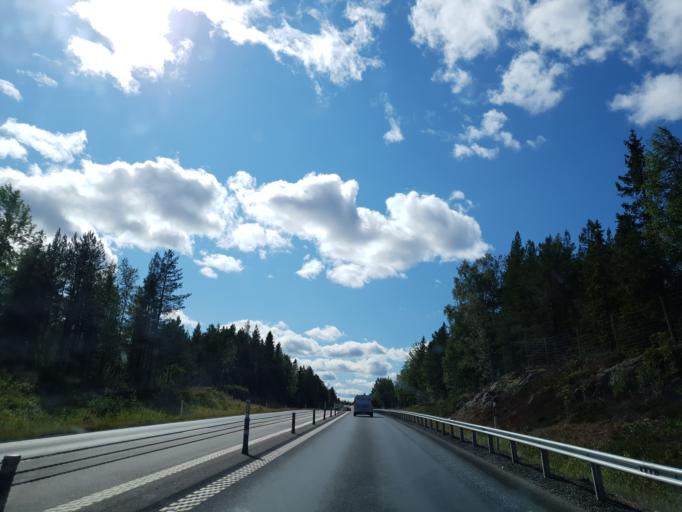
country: SE
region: Vaesterbotten
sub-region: Nordmalings Kommun
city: Nordmaling
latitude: 63.4963
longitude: 19.3225
